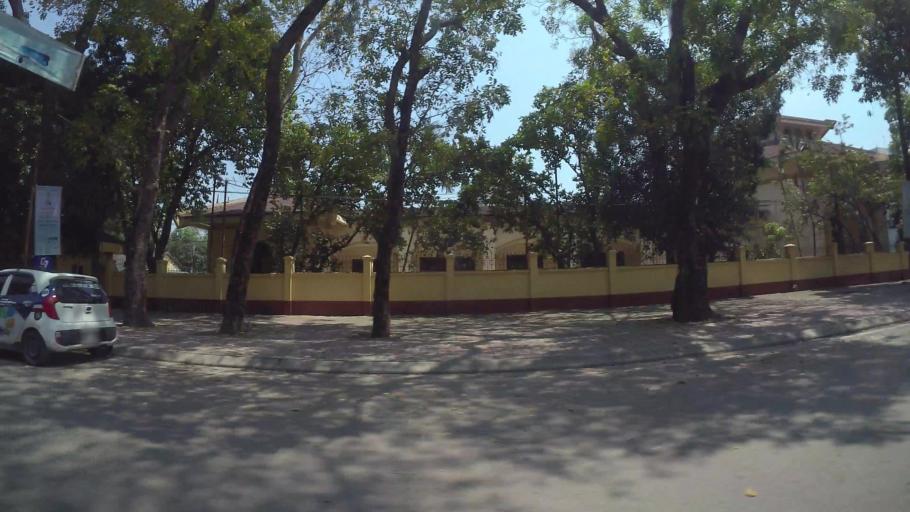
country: VN
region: Ha Noi
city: Hoan Kiem
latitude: 21.0447
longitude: 105.8828
